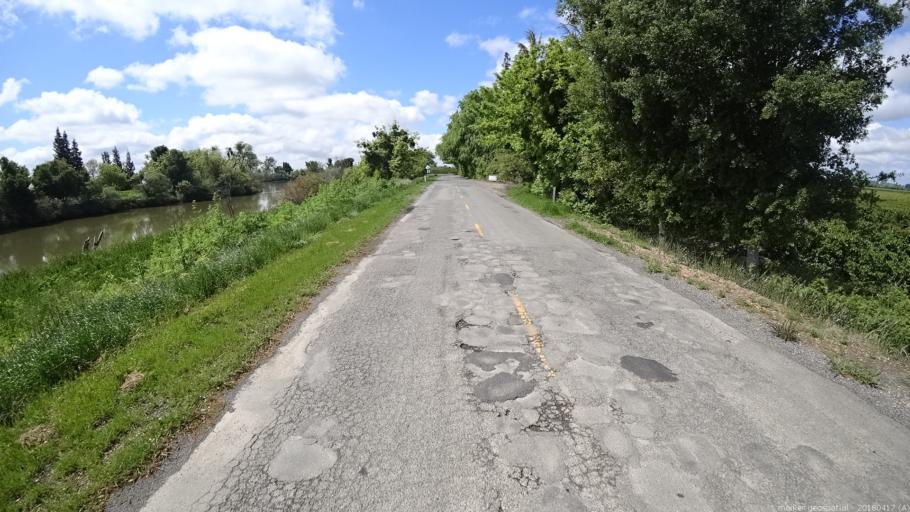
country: US
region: California
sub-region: Sacramento County
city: Walnut Grove
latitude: 38.2291
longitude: -121.5254
